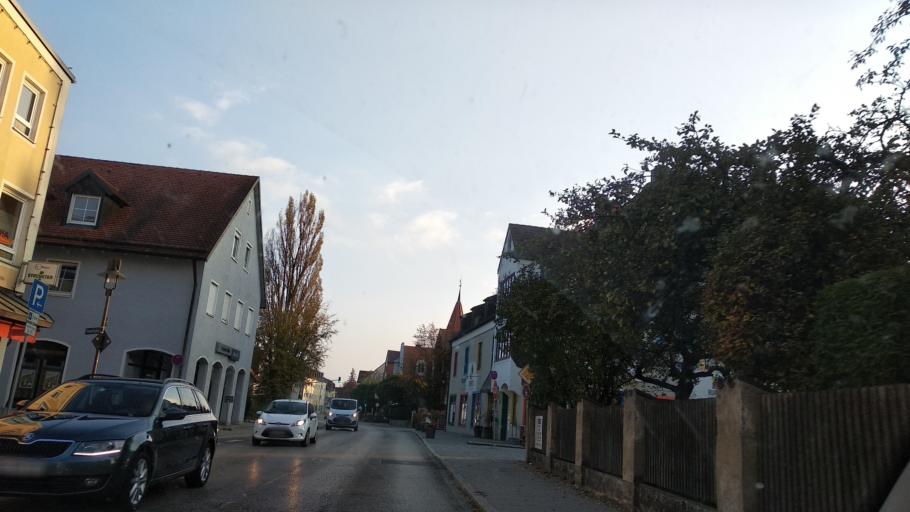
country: DE
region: Bavaria
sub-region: Upper Bavaria
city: Markt Schwaben
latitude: 48.1896
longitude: 11.8690
